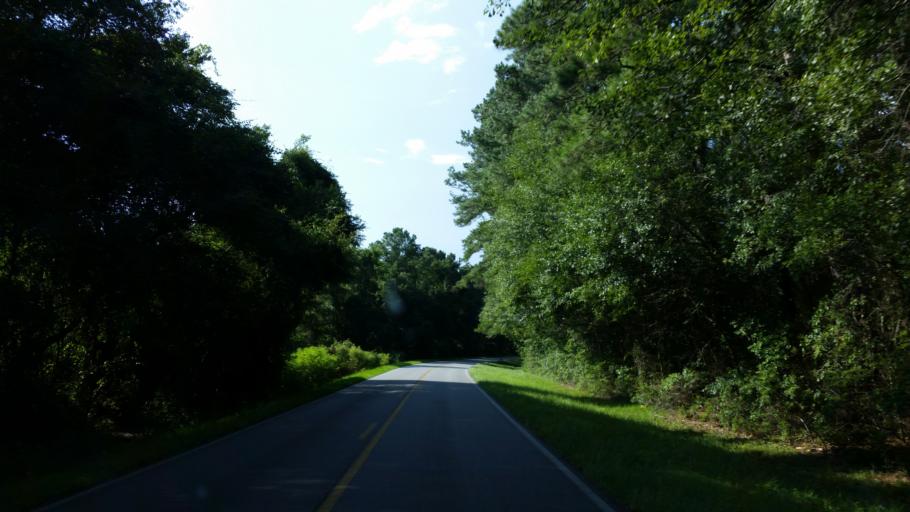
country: US
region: Georgia
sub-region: Lowndes County
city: Hahira
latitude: 30.9473
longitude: -83.4100
